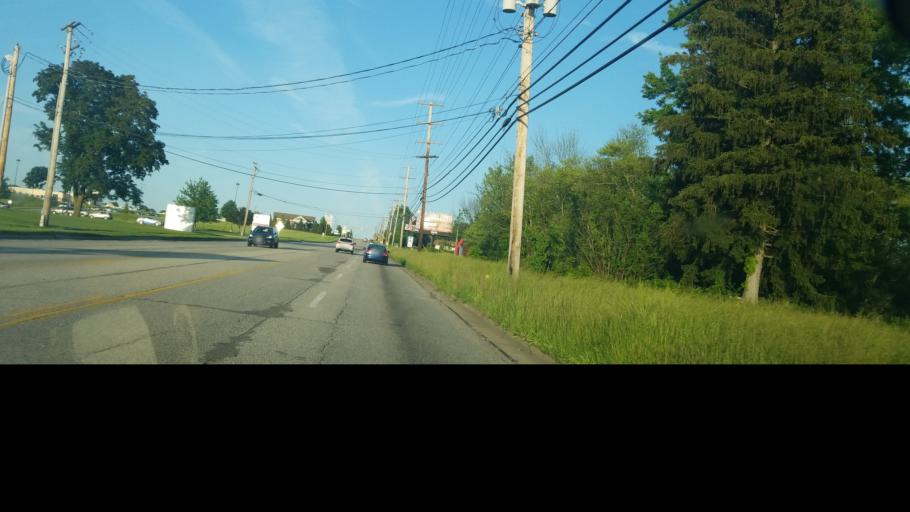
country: US
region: Ohio
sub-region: Mahoning County
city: Austintown
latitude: 41.0995
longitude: -80.7828
